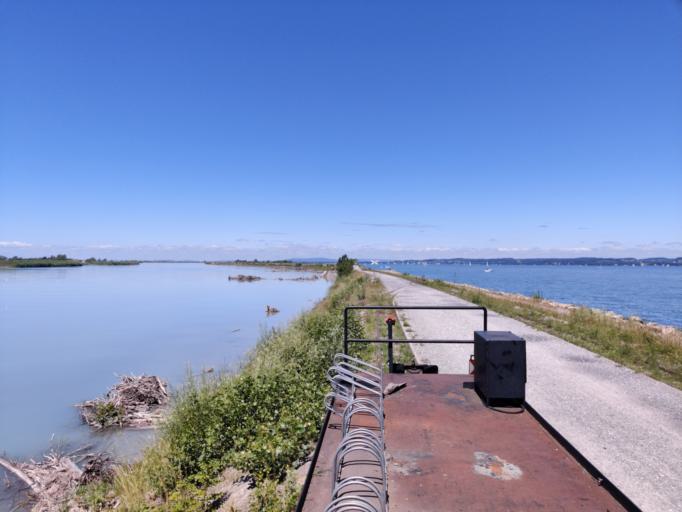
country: AT
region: Vorarlberg
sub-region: Politischer Bezirk Bregenz
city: Hard
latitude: 47.5065
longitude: 9.6692
